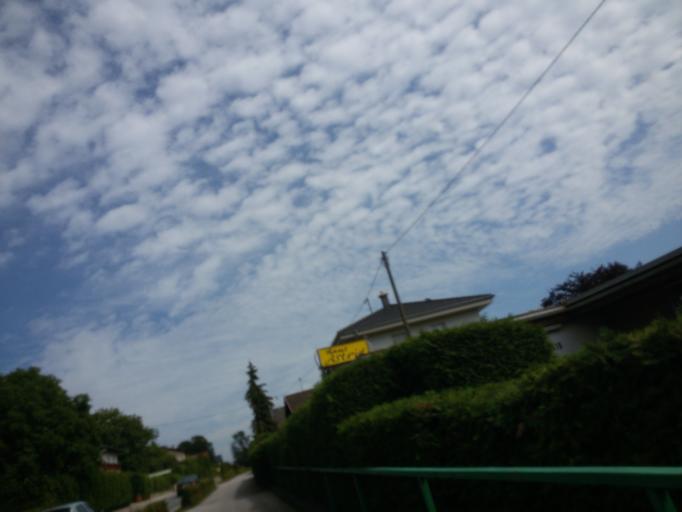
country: AT
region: Carinthia
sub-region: Politischer Bezirk Klagenfurt Land
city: Maria Worth
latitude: 46.6285
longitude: 14.1705
